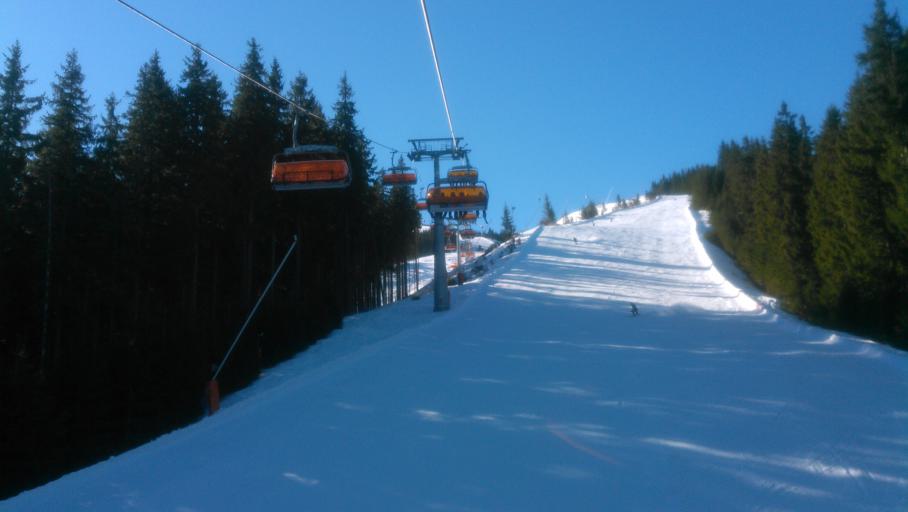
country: SK
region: Banskobystricky
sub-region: Okres Banska Bystrica
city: Brezno
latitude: 48.9221
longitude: 19.5975
